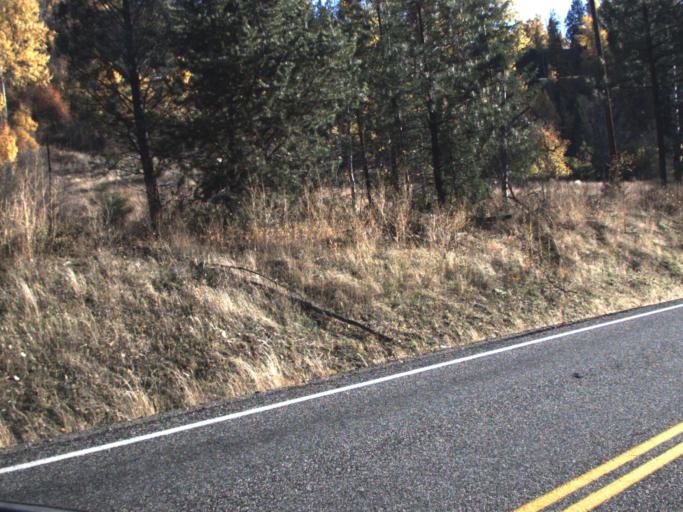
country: CA
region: British Columbia
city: Rossland
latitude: 48.9001
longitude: -117.7955
